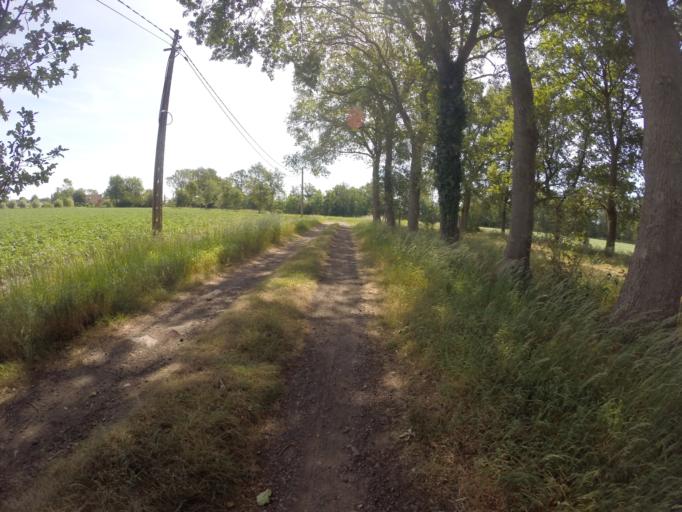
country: BE
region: Flanders
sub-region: Provincie West-Vlaanderen
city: Beernem
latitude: 51.1445
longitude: 3.3716
